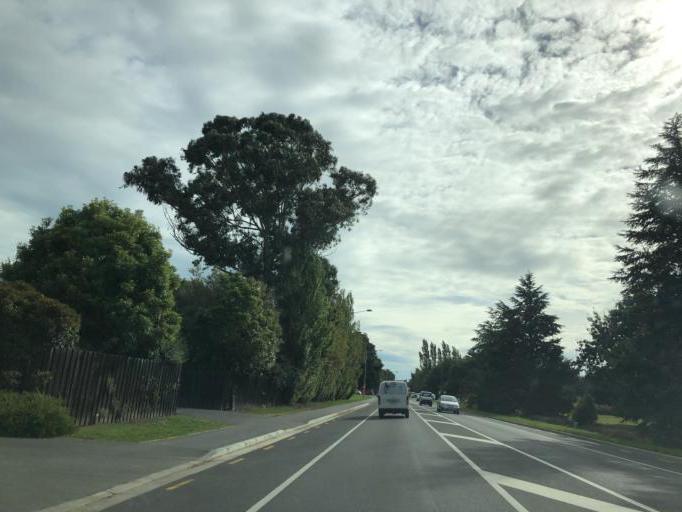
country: NZ
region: Canterbury
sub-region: Selwyn District
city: Lincoln
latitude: -43.6417
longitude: 172.4727
